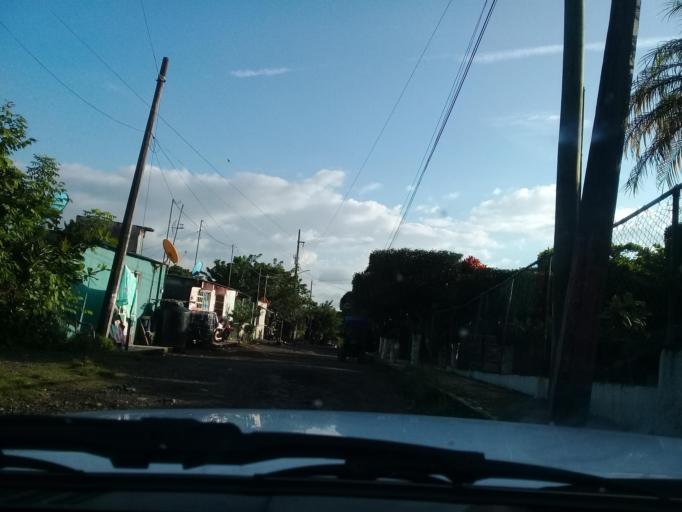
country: MX
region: Veracruz
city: Catemaco
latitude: 18.4244
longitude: -95.1013
